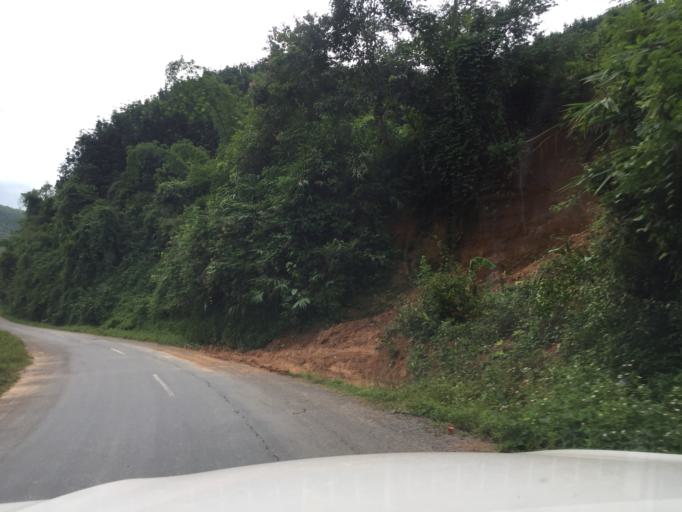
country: LA
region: Oudomxai
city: Muang La
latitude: 21.1072
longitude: 102.2323
